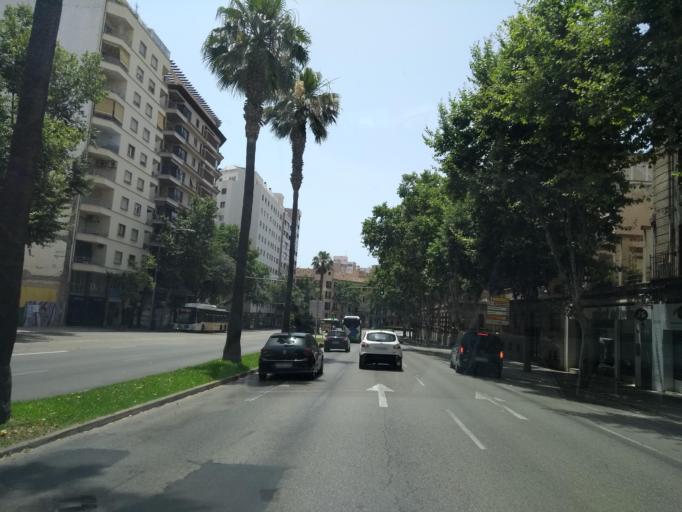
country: ES
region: Balearic Islands
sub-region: Illes Balears
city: Palma
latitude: 39.5778
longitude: 2.6480
